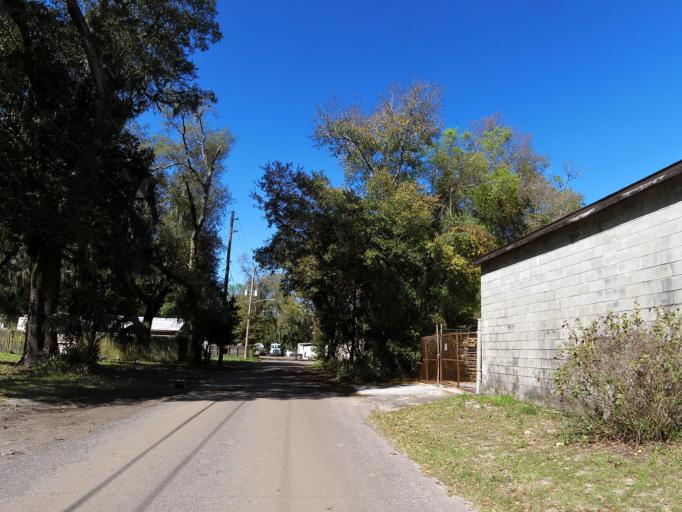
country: US
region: Florida
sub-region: Duval County
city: Jacksonville
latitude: 30.3619
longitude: -81.6462
